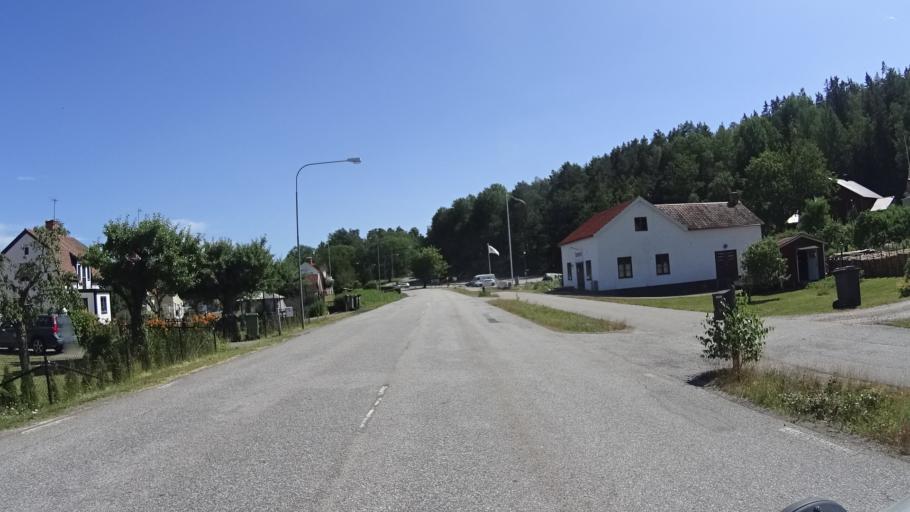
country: SE
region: Kalmar
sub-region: Vasterviks Kommun
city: Gamleby
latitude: 57.9063
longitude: 16.4116
